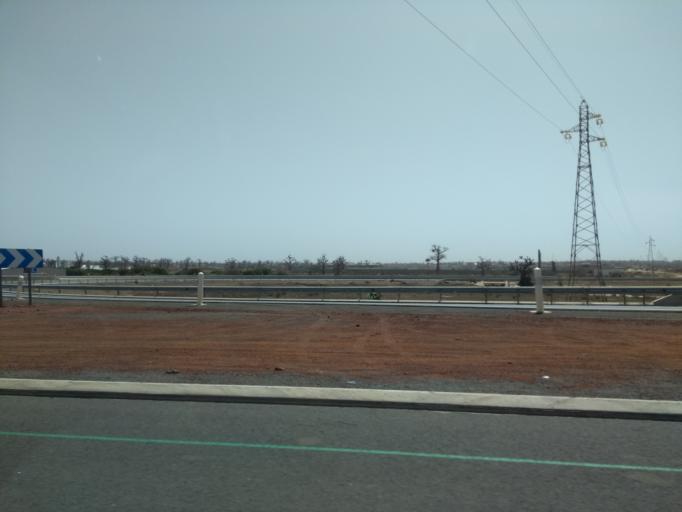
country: SN
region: Thies
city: Pout
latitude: 14.7294
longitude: -17.1572
